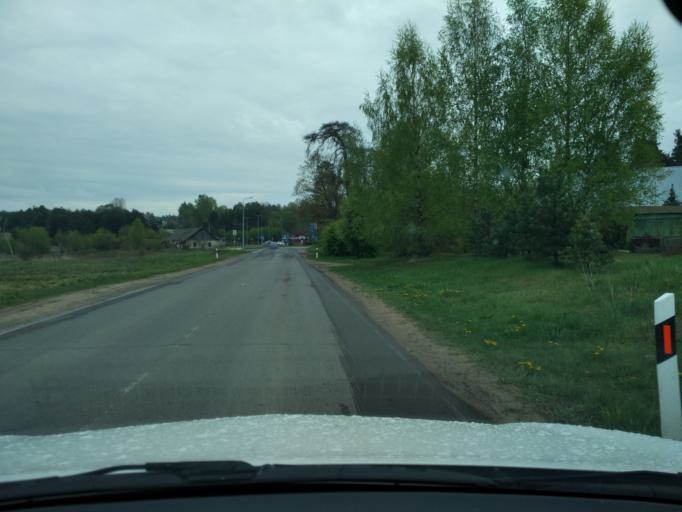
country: LT
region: Vilnius County
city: Rasos
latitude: 54.7378
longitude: 25.4012
